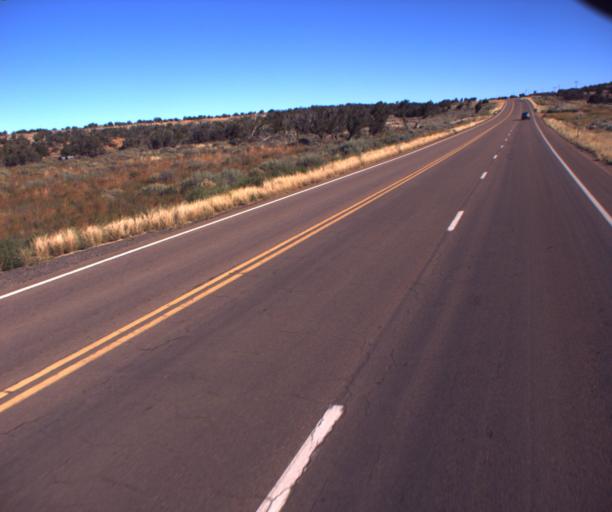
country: US
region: Arizona
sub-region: Navajo County
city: Snowflake
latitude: 34.5347
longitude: -110.0810
